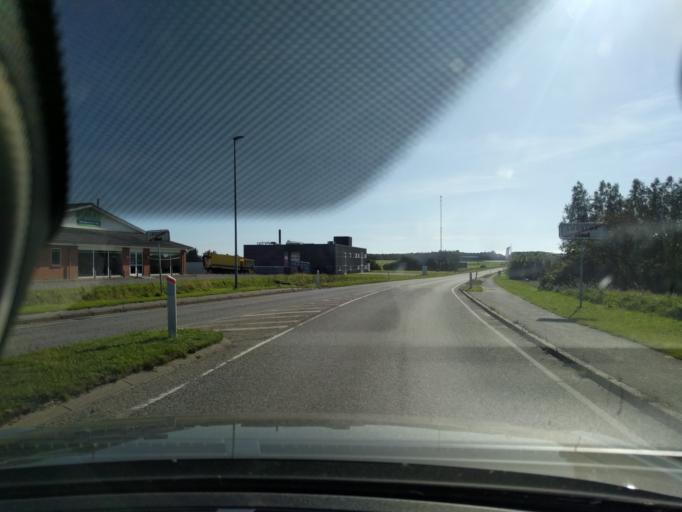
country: DK
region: North Denmark
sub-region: Vesthimmerland Kommune
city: Logstor
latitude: 56.9559
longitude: 9.2637
